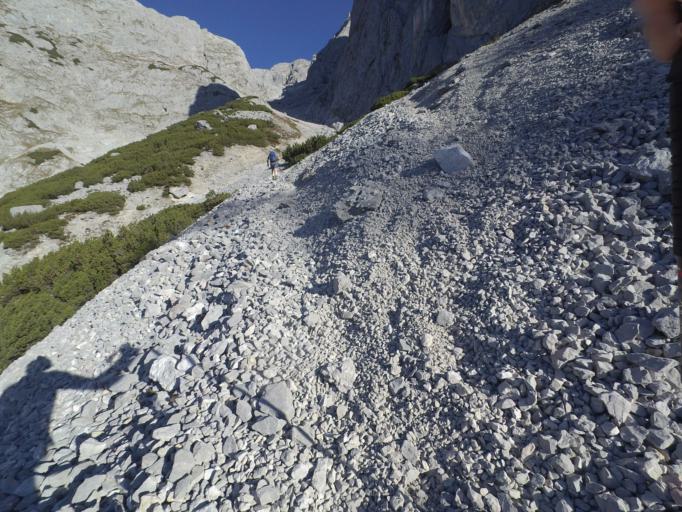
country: AT
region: Salzburg
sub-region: Politischer Bezirk Sankt Johann im Pongau
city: Werfenweng
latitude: 47.4914
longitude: 13.2328
